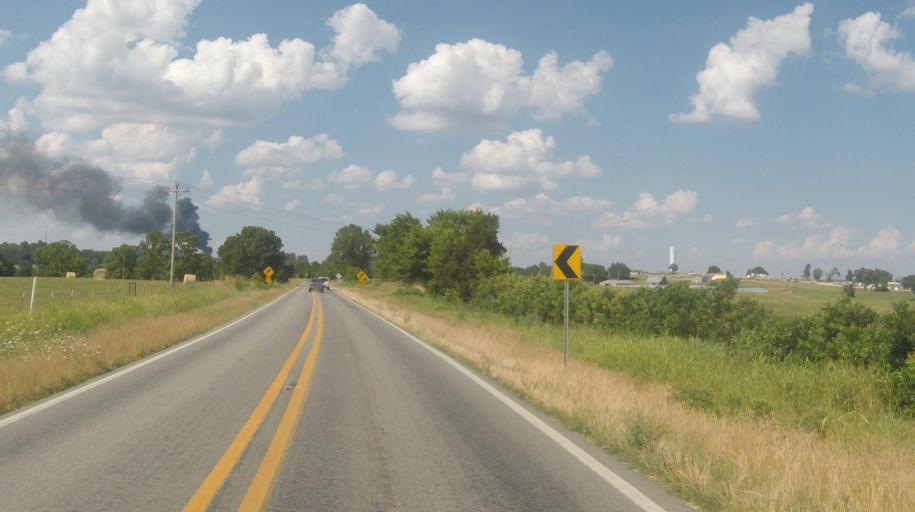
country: US
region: Arkansas
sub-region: Carroll County
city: Eureka Springs
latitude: 36.2627
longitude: -93.7709
